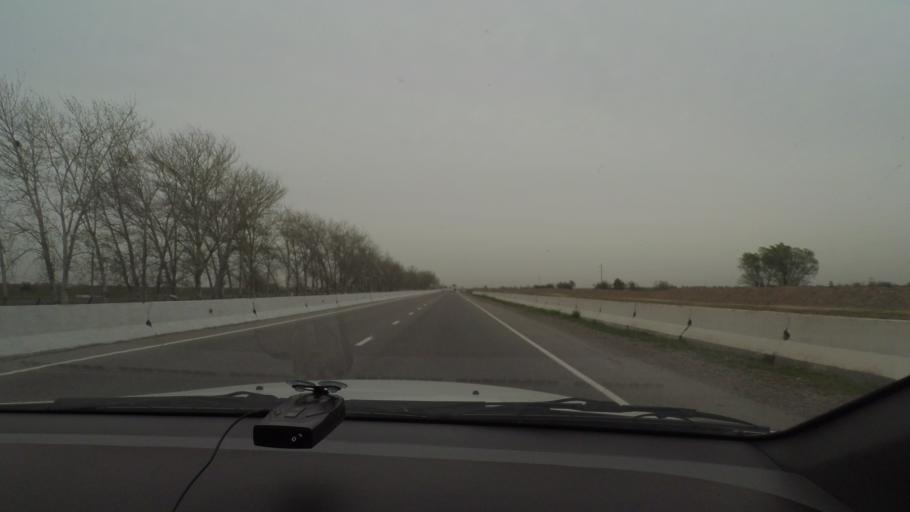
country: UZ
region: Jizzax
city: Dustlik
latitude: 40.4090
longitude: 68.1998
